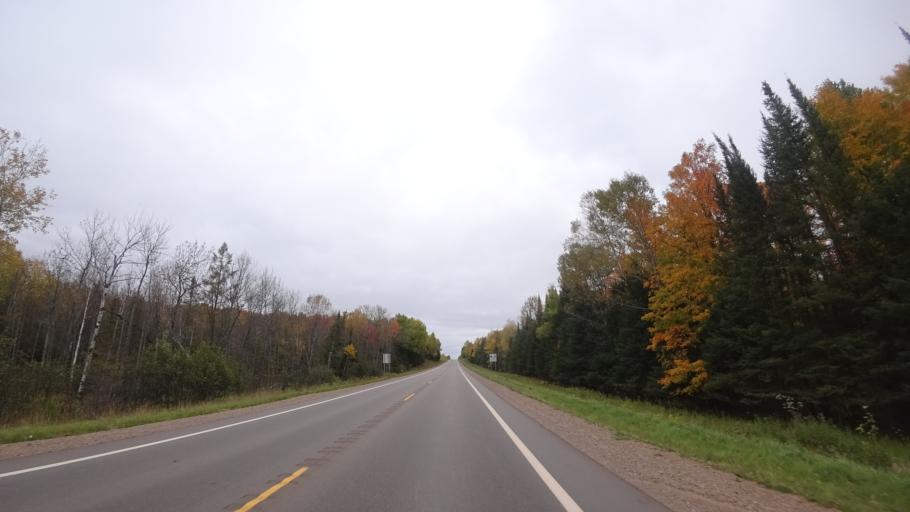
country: US
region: Michigan
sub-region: Iron County
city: Crystal Falls
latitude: 46.1782
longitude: -88.0480
